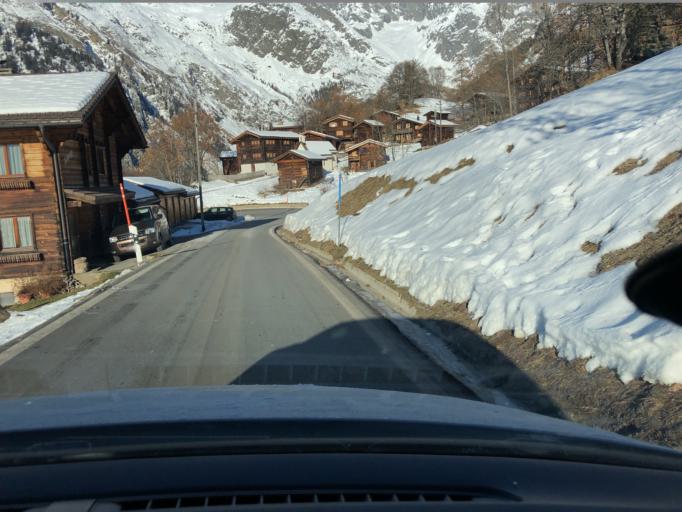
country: CH
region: Valais
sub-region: Goms District
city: Fiesch
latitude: 46.4330
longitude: 8.1477
